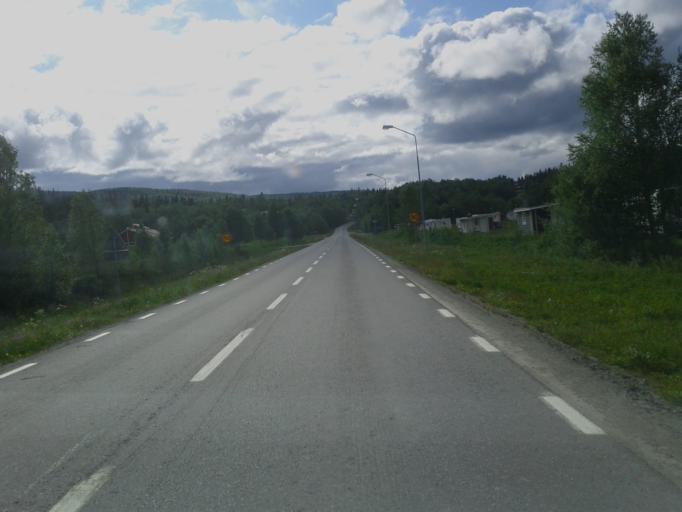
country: NO
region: Nordland
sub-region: Rana
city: Mo i Rana
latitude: 65.7106
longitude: 15.2466
